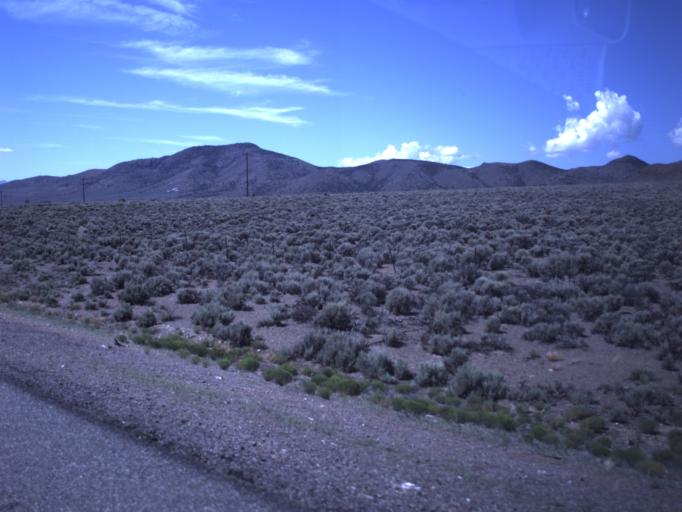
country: US
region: Utah
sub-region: Piute County
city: Junction
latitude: 38.2840
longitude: -112.2249
